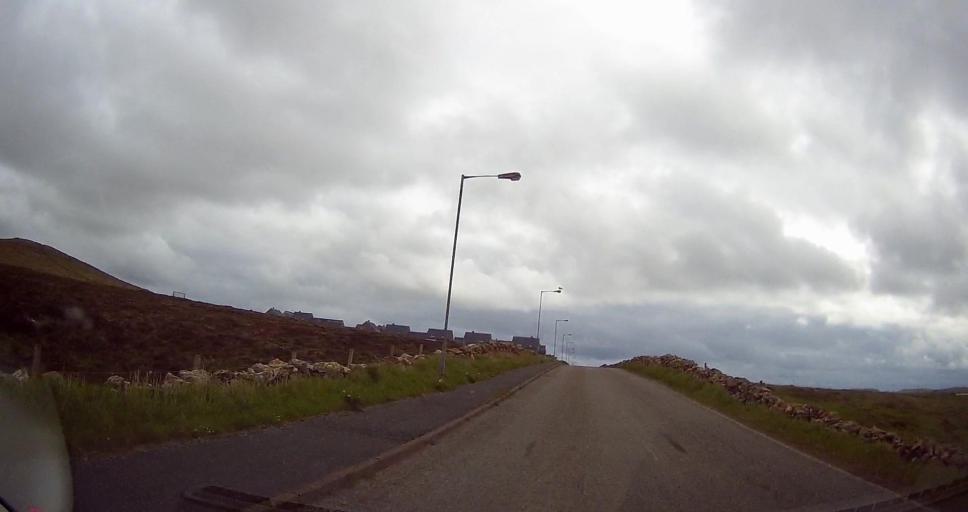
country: GB
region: Scotland
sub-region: Shetland Islands
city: Shetland
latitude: 60.7620
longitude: -0.8688
